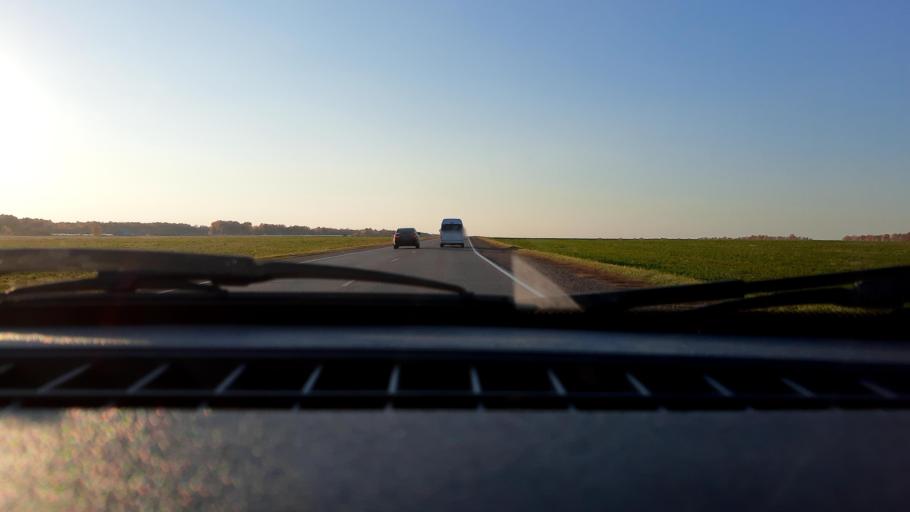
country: RU
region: Bashkortostan
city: Avdon
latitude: 54.8222
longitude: 55.6637
